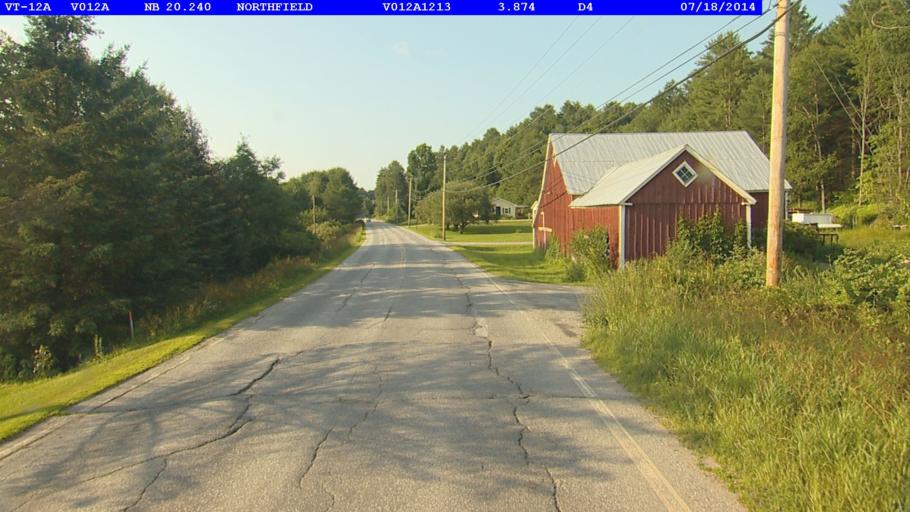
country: US
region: Vermont
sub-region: Washington County
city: Northfield
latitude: 44.1265
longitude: -72.6629
